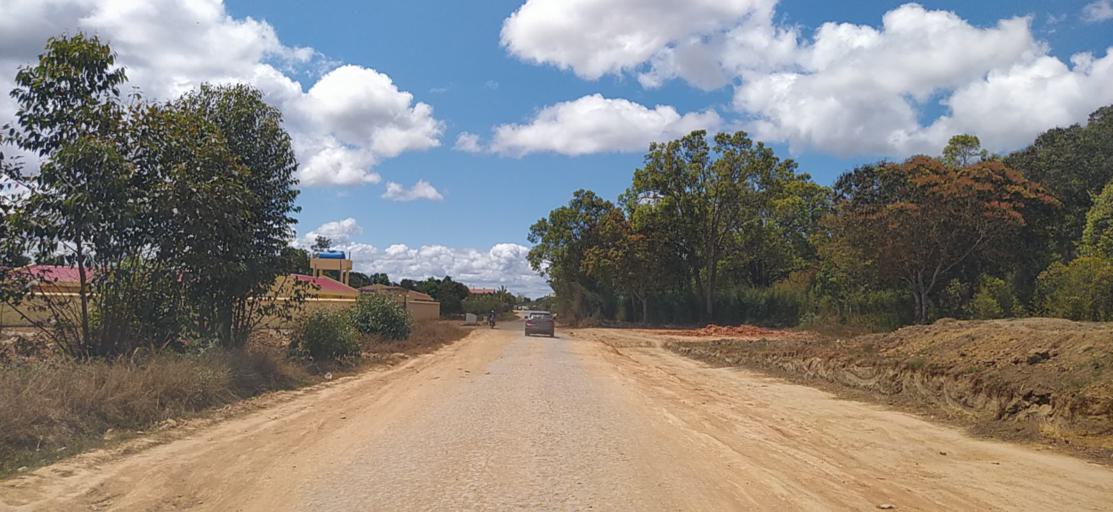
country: MG
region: Alaotra Mangoro
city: Moramanga
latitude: -18.7039
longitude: 48.2714
